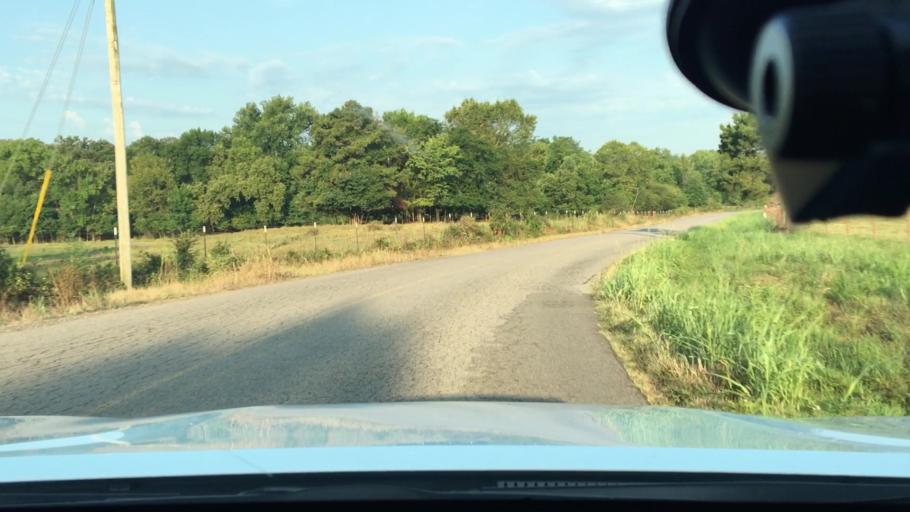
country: US
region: Arkansas
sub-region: Johnson County
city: Coal Hill
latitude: 35.3659
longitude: -93.5928
